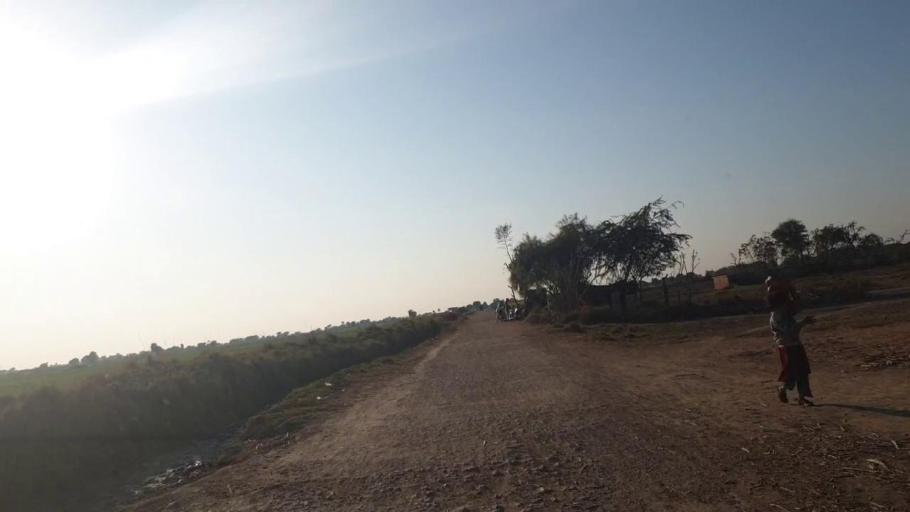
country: PK
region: Sindh
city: Shahpur Chakar
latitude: 26.0606
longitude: 68.6687
